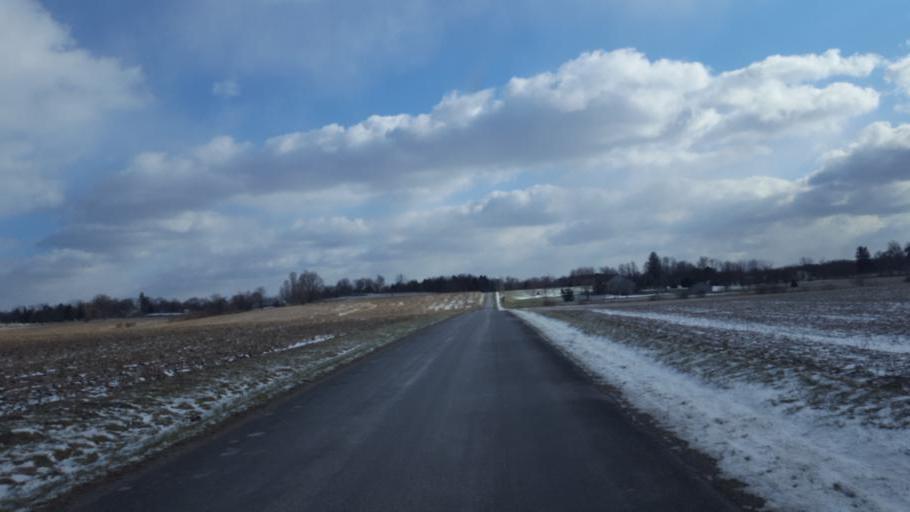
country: US
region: Ohio
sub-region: Crawford County
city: Galion
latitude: 40.7155
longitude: -82.7224
